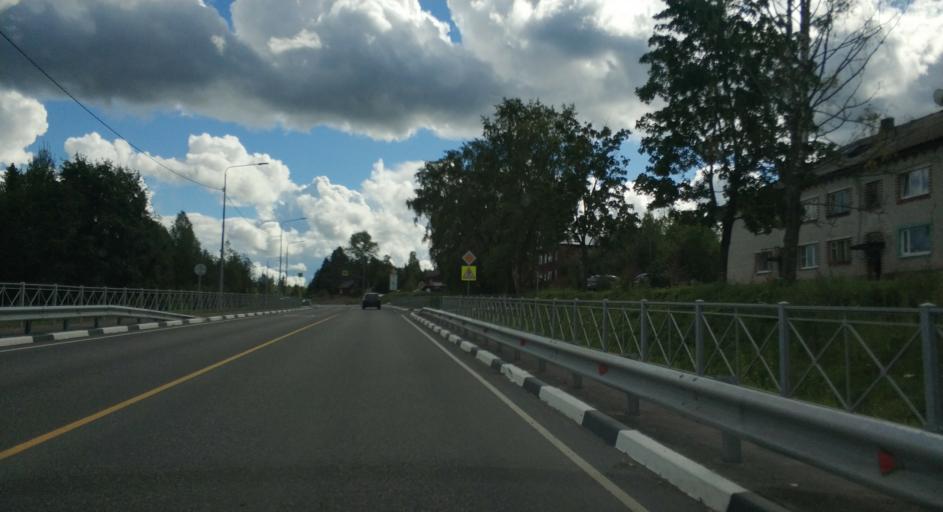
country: RU
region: Republic of Karelia
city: Ruskeala
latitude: 61.9334
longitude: 30.5924
